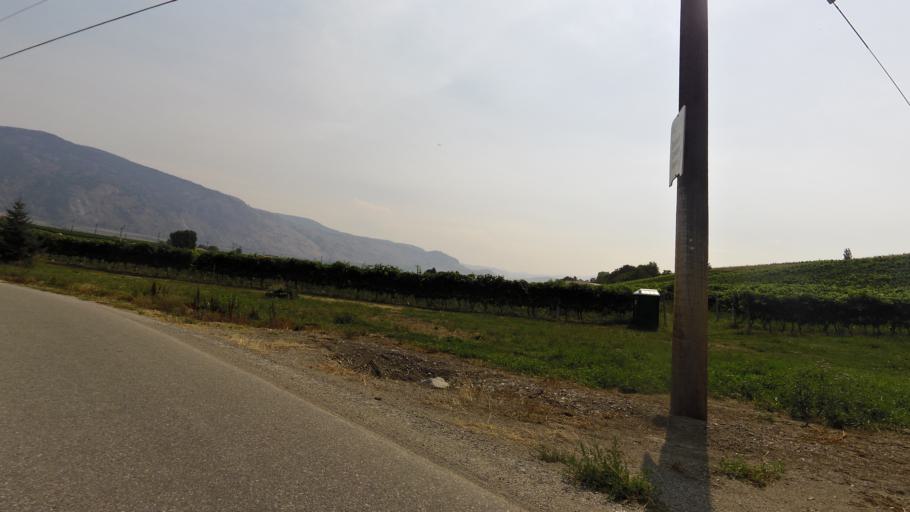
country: CA
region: British Columbia
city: Osoyoos
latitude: 49.0523
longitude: -119.5079
